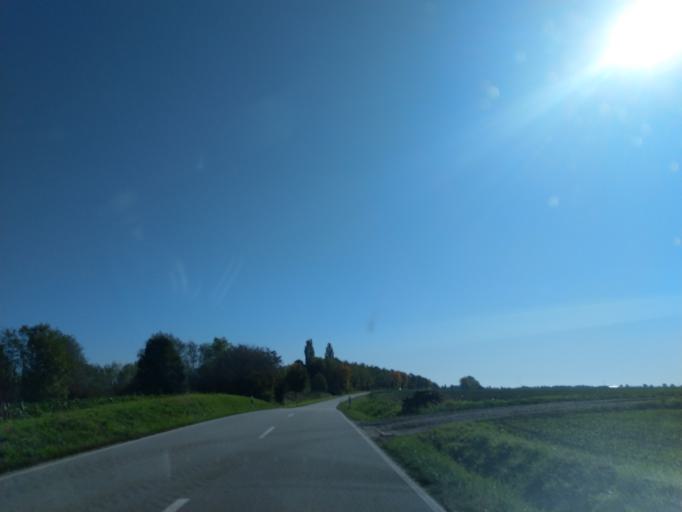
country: DE
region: Bavaria
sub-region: Lower Bavaria
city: Mariaposching
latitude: 48.8260
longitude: 12.7822
